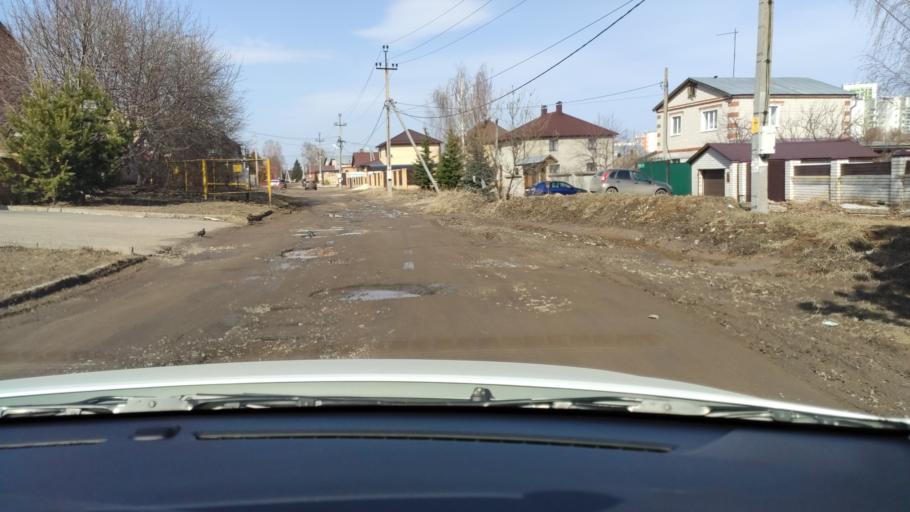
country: RU
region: Tatarstan
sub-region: Gorod Kazan'
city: Kazan
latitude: 55.7866
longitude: 49.2471
